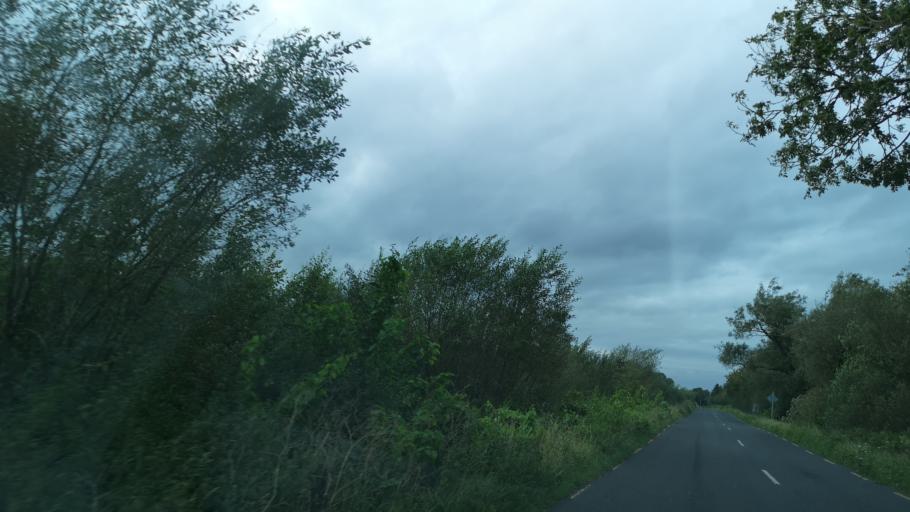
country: IE
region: Leinster
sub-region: Uibh Fhaili
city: Ferbane
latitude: 53.2127
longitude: -7.7895
